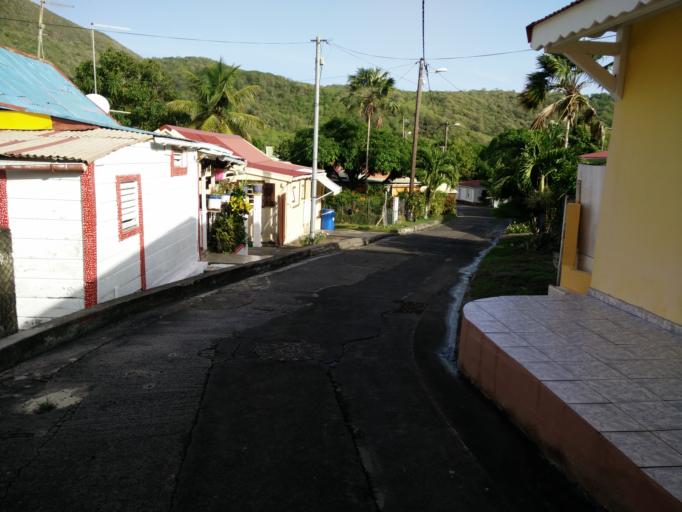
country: GP
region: Guadeloupe
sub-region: Guadeloupe
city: Terre-de-Bas
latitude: 15.8577
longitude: -61.6233
